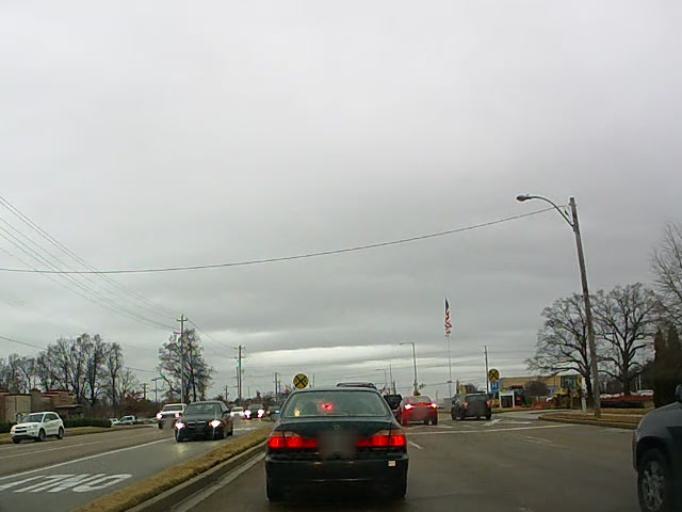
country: US
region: Tennessee
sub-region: Shelby County
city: Collierville
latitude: 35.0500
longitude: -89.7325
